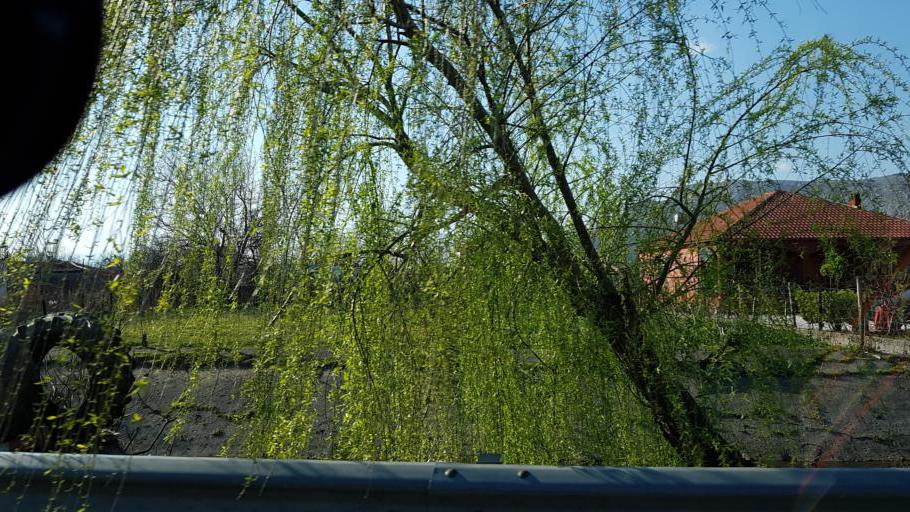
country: AL
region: Shkoder
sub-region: Rrethi i Shkodres
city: Vau i Dejes
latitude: 41.9957
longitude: 19.6120
